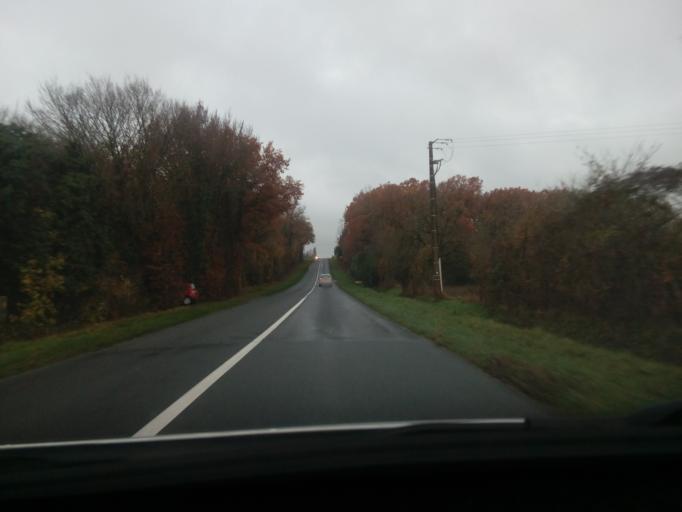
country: FR
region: Poitou-Charentes
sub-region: Departement de la Charente
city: Barbezieux-Saint-Hilaire
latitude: 45.4617
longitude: -0.2078
